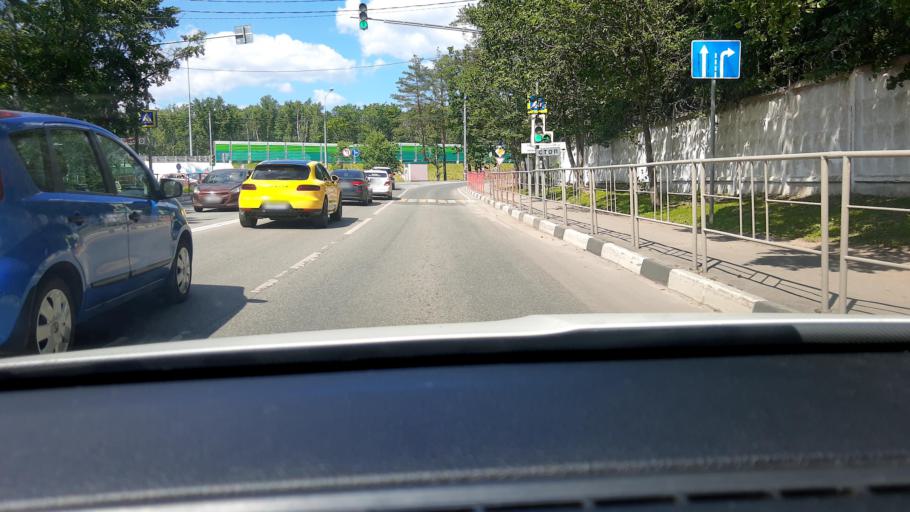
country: RU
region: Moskovskaya
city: Odintsovo
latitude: 55.6897
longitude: 37.2564
